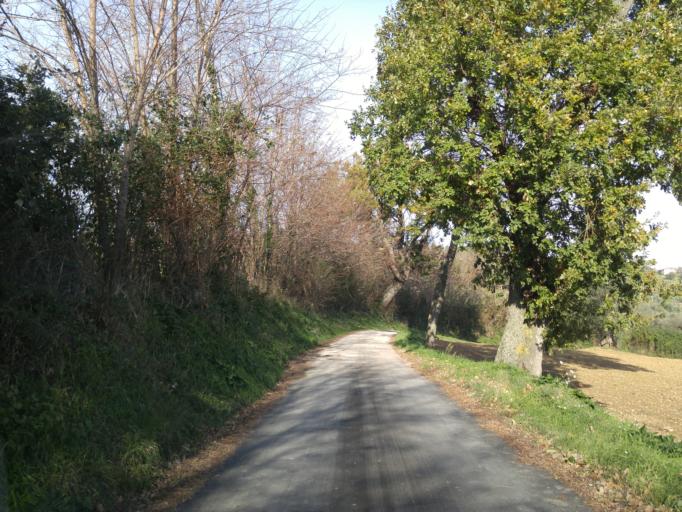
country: IT
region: The Marches
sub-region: Provincia di Pesaro e Urbino
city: Saltara
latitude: 43.7611
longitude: 12.9006
